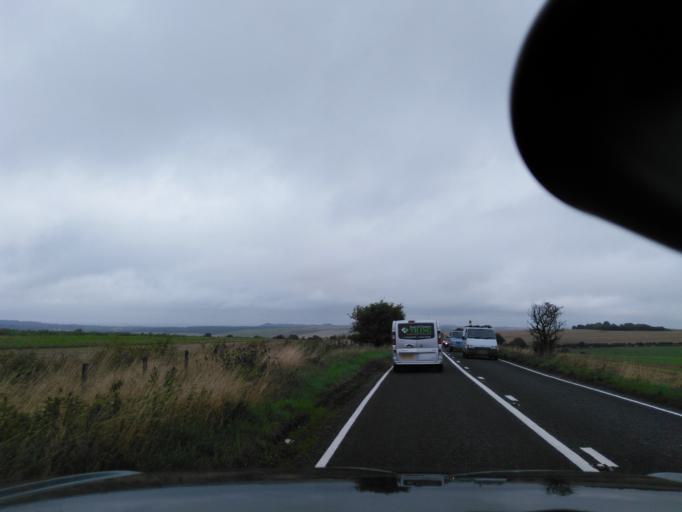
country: GB
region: England
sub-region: Wiltshire
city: Chicklade
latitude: 51.1387
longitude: -2.1622
